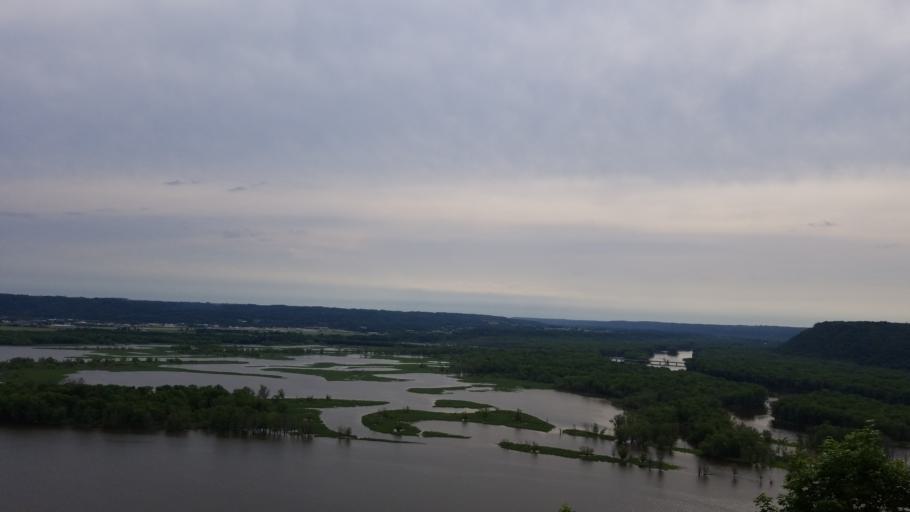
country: US
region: Wisconsin
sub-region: Crawford County
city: Prairie du Chien
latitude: 42.9964
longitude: -91.1629
